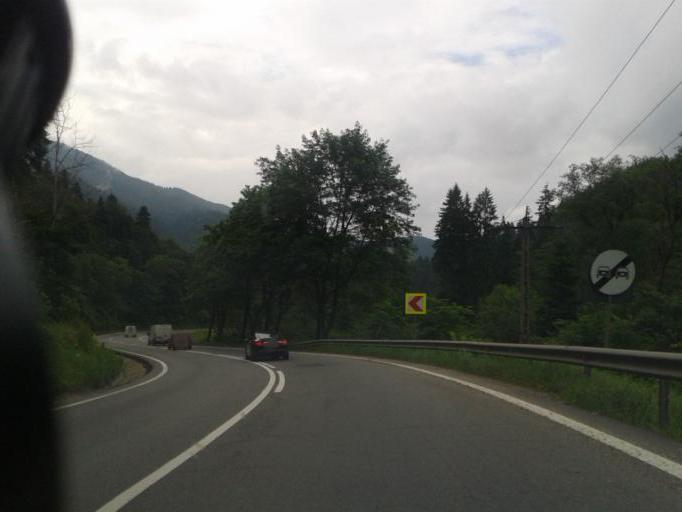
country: RO
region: Brasov
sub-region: Oras Predeal
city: Predeal
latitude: 45.5398
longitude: 25.5888
